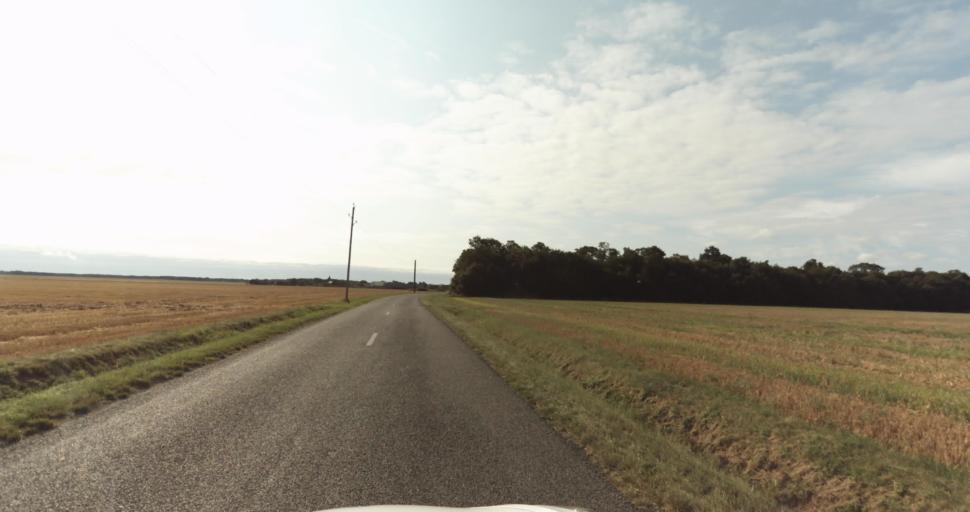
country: FR
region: Haute-Normandie
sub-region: Departement de l'Eure
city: Nonancourt
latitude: 48.8123
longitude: 1.1334
